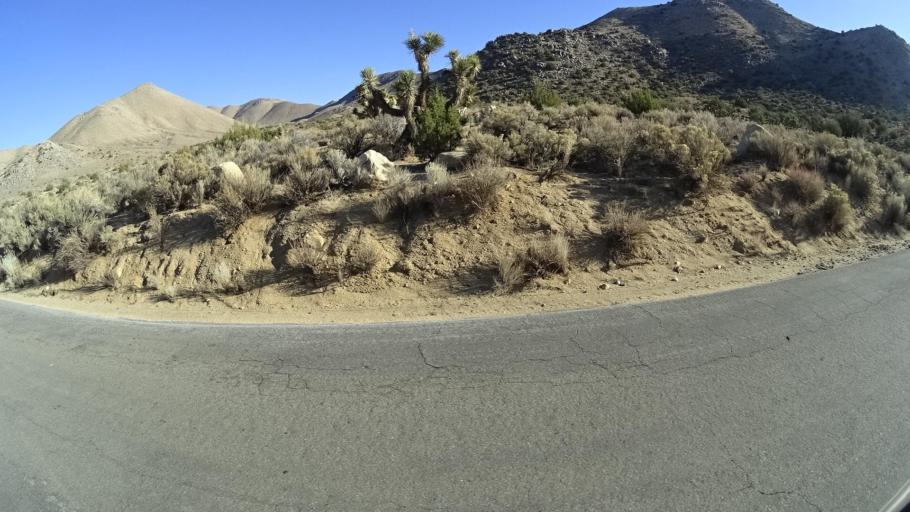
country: US
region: California
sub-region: Kern County
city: Weldon
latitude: 35.5853
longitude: -118.2458
